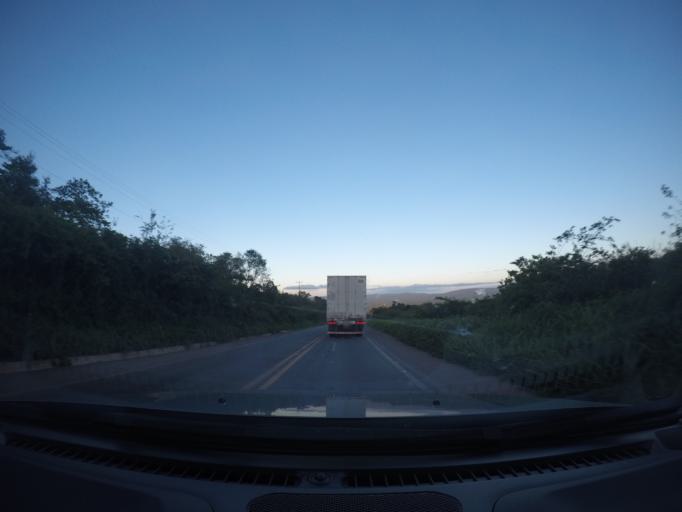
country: BR
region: Bahia
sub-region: Seabra
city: Seabra
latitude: -12.4138
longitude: -41.9784
